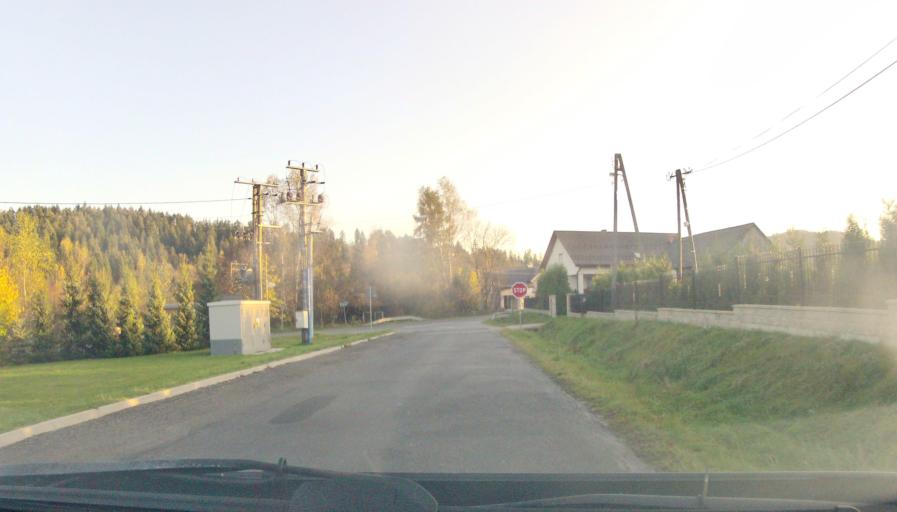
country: PL
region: Lesser Poland Voivodeship
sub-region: Powiat suski
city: Kukow
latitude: 49.7464
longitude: 19.4661
